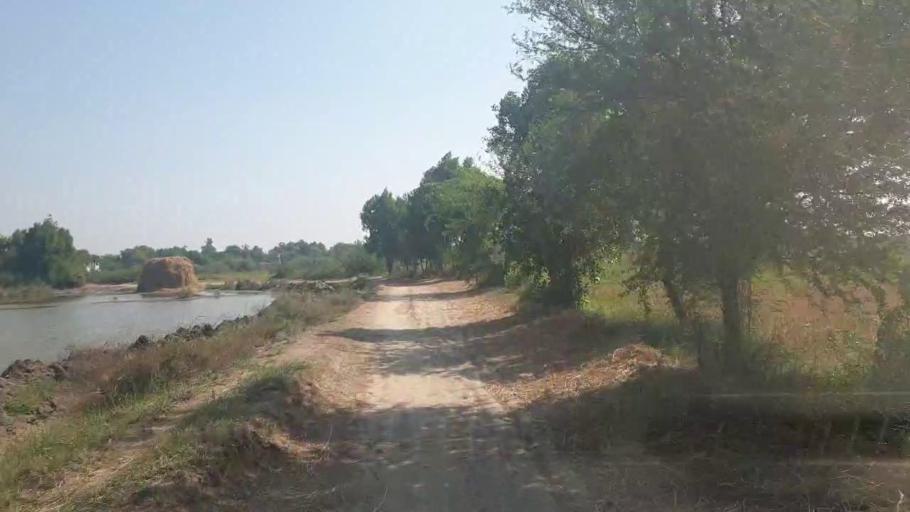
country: PK
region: Sindh
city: Badin
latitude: 24.6829
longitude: 68.8752
